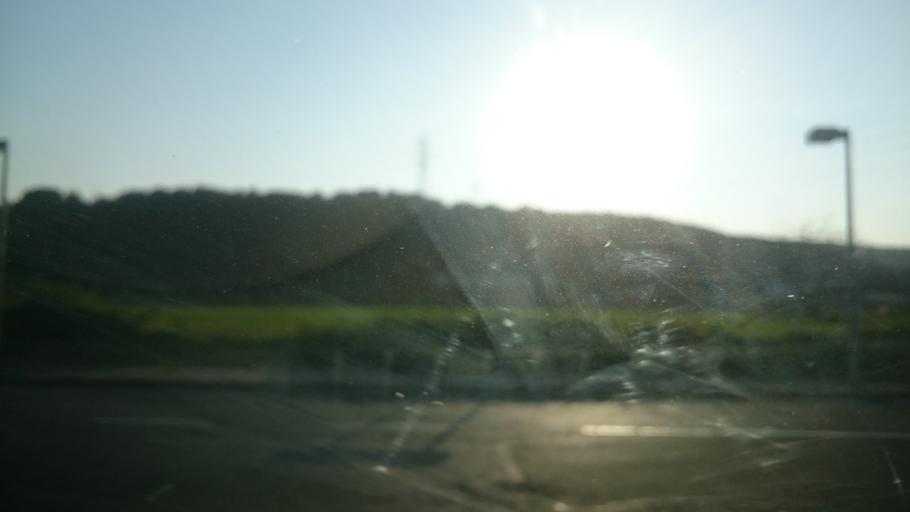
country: ES
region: Catalonia
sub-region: Provincia de Barcelona
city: Cubelles
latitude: 41.2166
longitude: 1.6626
